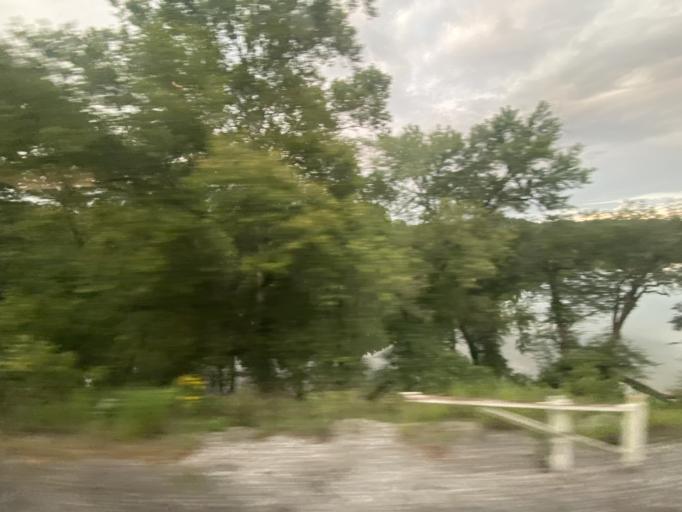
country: US
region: West Virginia
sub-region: Mineral County
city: Fort Ashby
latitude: 39.5284
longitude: -78.5887
